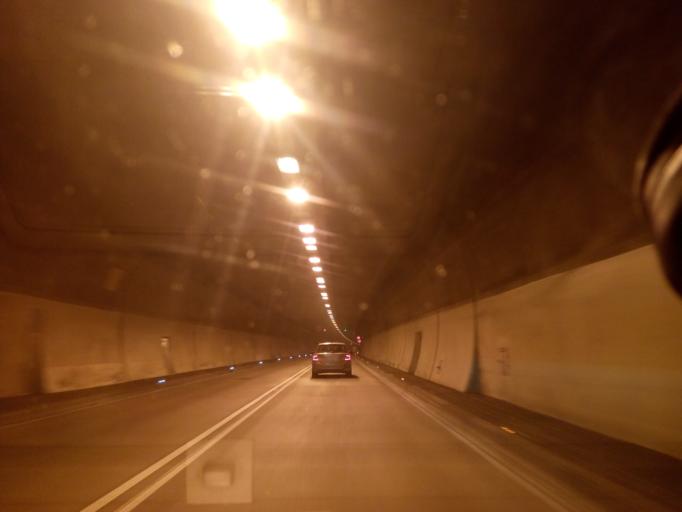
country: SK
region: Kosicky
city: Krompachy
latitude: 48.9964
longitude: 20.9050
